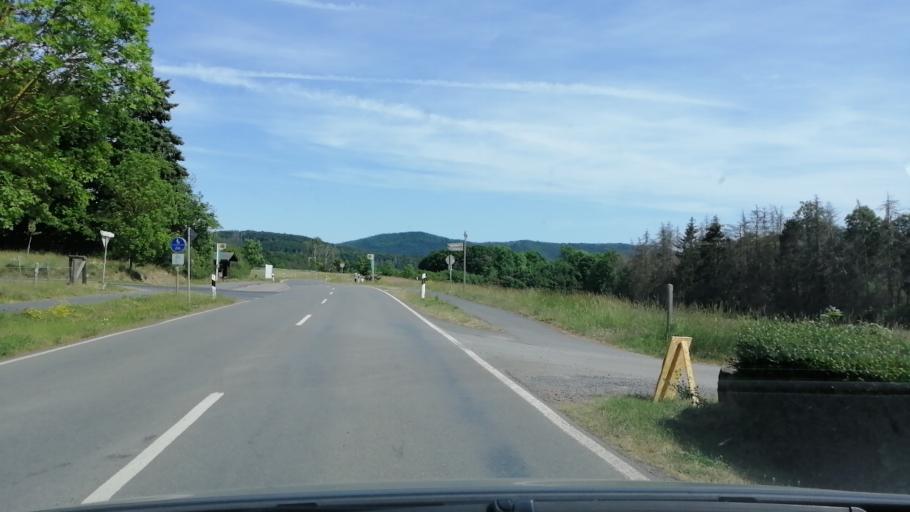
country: DE
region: Hesse
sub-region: Regierungsbezirk Kassel
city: Waldeck
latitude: 51.1783
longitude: 9.0378
